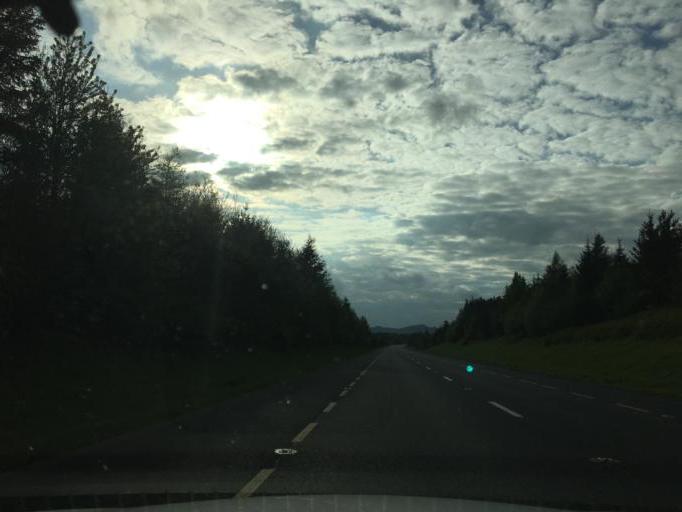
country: IE
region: Leinster
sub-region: Loch Garman
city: Enniscorthy
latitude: 52.3532
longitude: -6.6748
